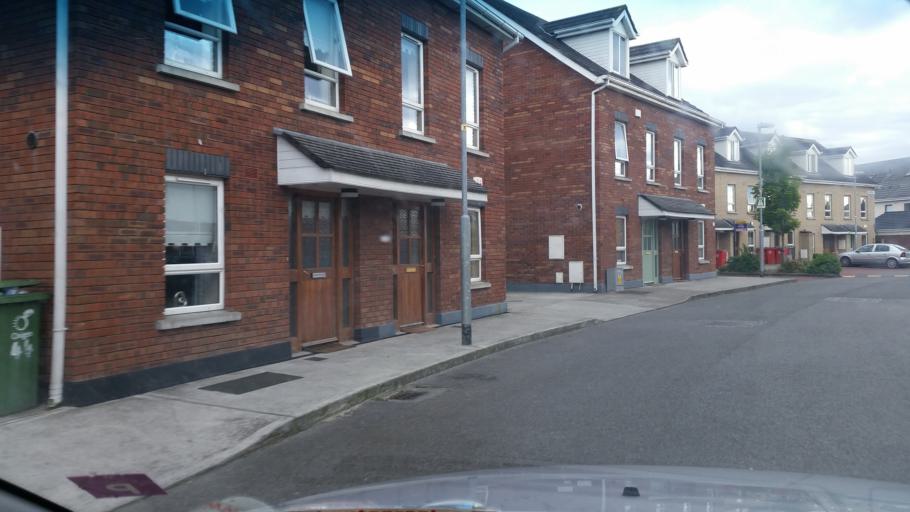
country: IE
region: Leinster
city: Donaghmede
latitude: 53.3995
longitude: -6.1504
